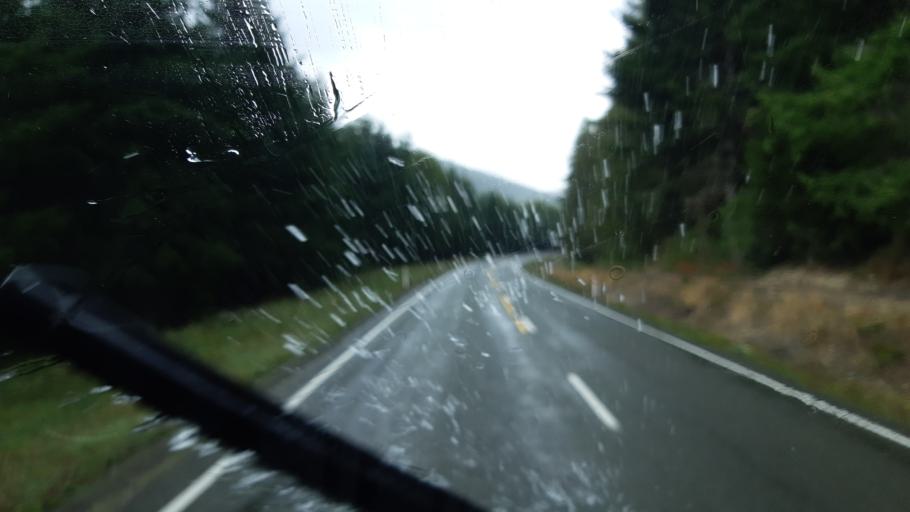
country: NZ
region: Tasman
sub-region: Tasman District
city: Wakefield
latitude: -41.4778
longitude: 172.8697
